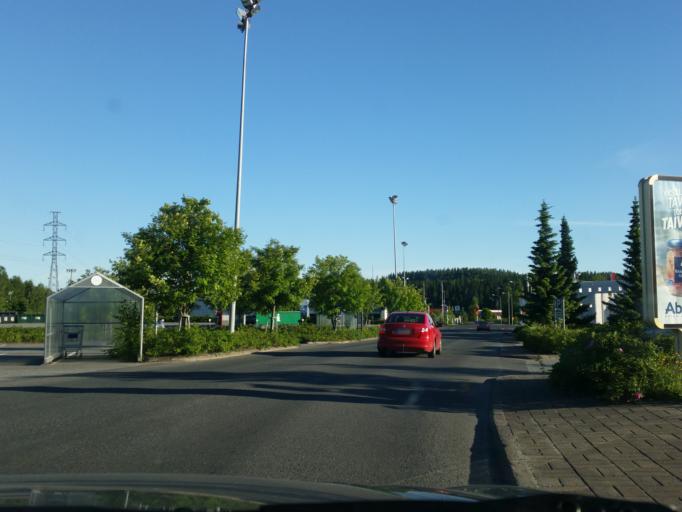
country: FI
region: Northern Savo
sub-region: Kuopio
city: Kuopio
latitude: 62.8638
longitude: 27.6149
